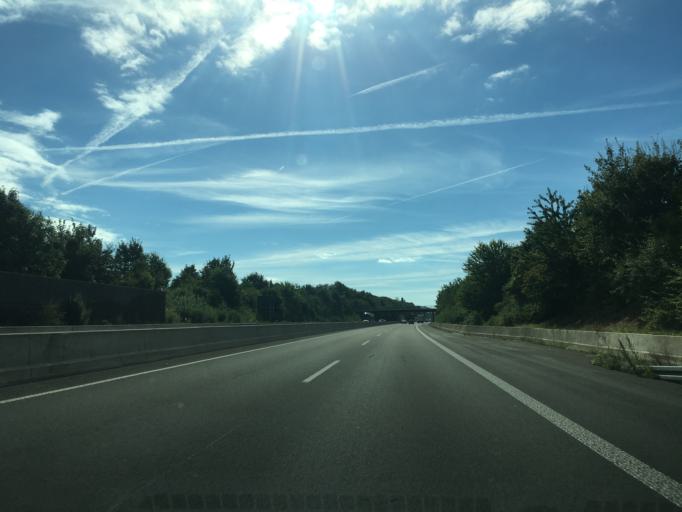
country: DE
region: North Rhine-Westphalia
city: Buende
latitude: 52.1857
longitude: 8.5851
